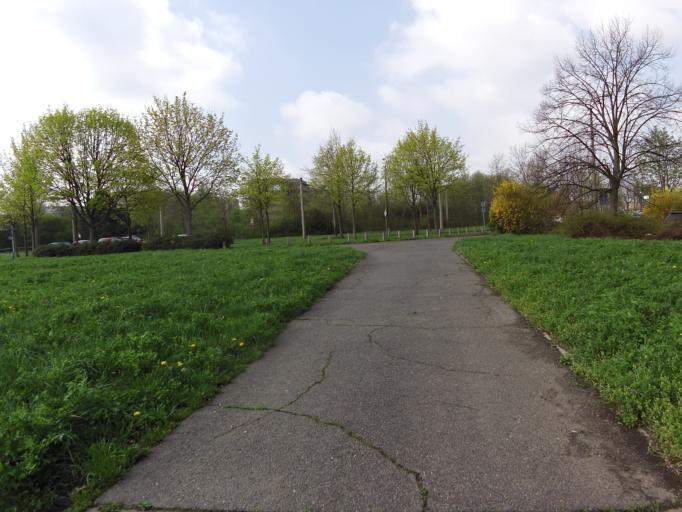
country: DE
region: Saxony
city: Markranstadt
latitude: 51.3232
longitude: 12.2678
